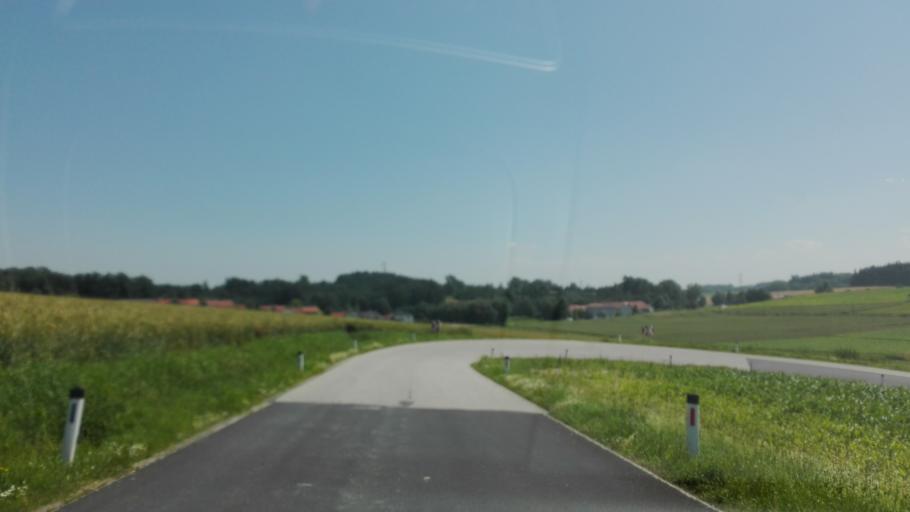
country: AT
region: Upper Austria
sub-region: Politischer Bezirk Grieskirchen
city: Grieskirchen
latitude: 48.3458
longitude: 13.8772
